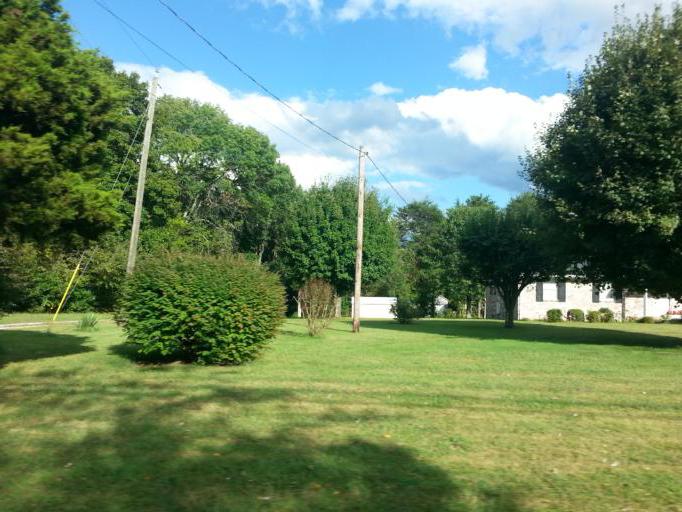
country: US
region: Tennessee
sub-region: Knox County
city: Mascot
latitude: 36.1008
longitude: -83.8152
